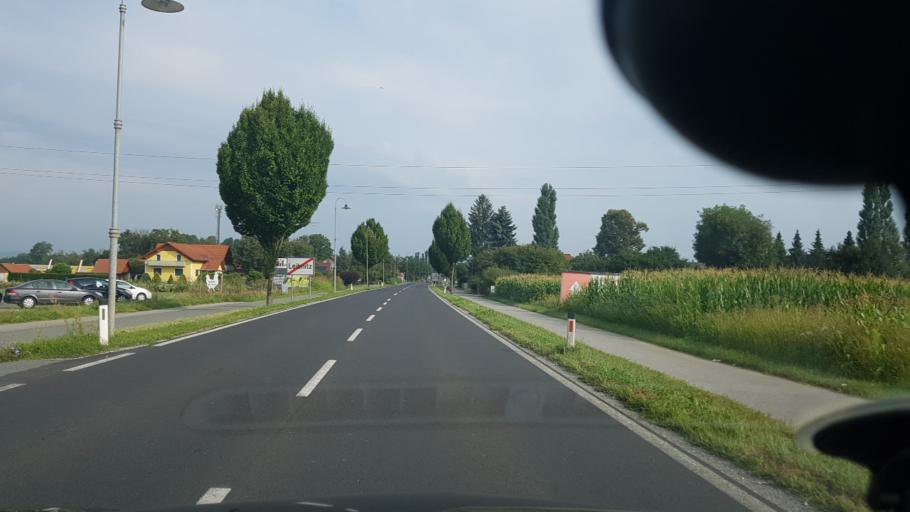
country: AT
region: Styria
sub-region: Politischer Bezirk Leibnitz
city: Kaindorf an der Sulm
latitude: 46.7994
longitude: 15.5571
